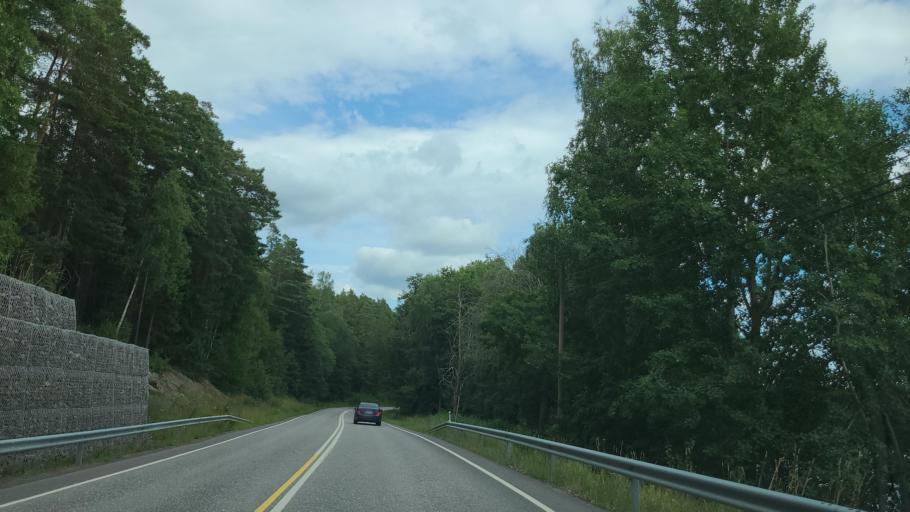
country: FI
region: Varsinais-Suomi
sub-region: Turku
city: Rymaettylae
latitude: 60.3847
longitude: 21.9205
